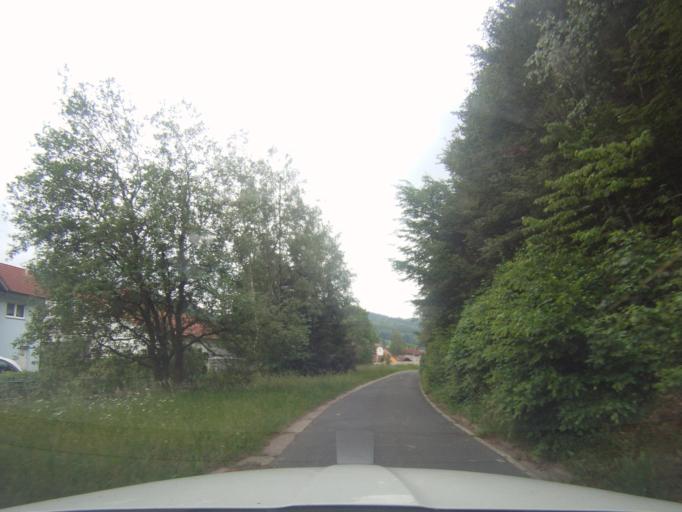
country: DE
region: Thuringia
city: Frauenwald
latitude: 50.5239
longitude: 10.8779
